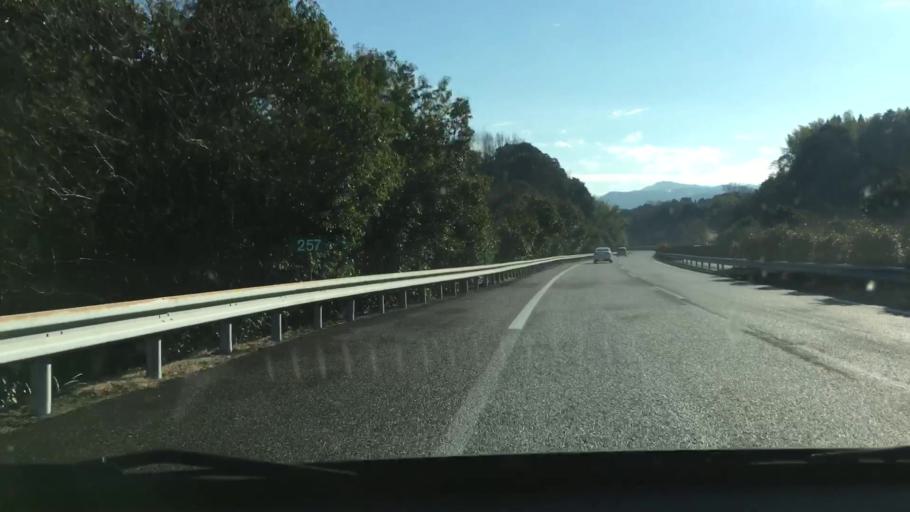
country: JP
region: Kumamoto
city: Hitoyoshi
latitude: 32.1938
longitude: 130.7778
